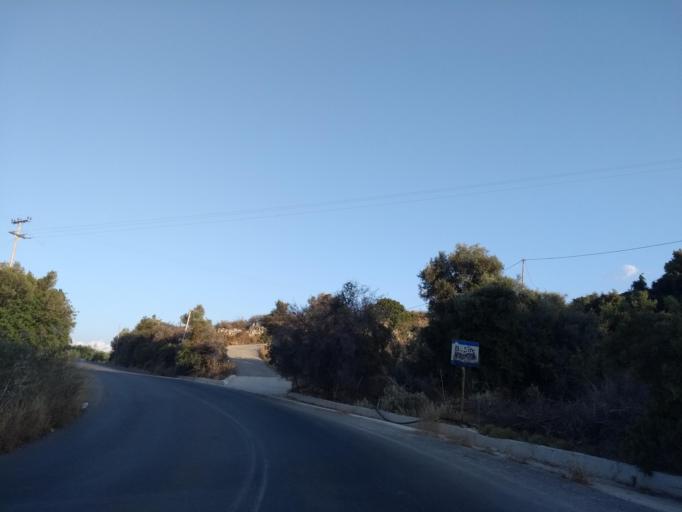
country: GR
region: Crete
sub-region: Nomos Chanias
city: Kalivai
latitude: 35.4215
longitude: 24.1856
